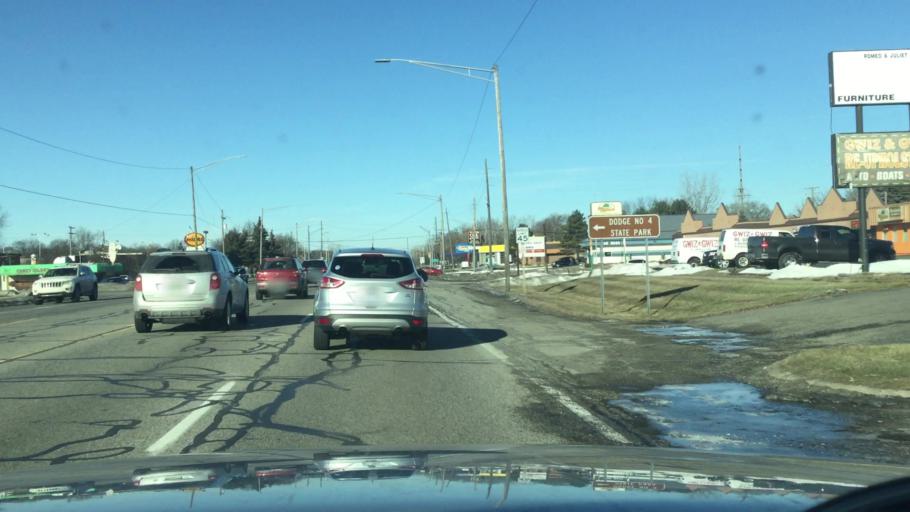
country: US
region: Michigan
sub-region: Oakland County
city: Keego Harbor
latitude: 42.6401
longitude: -83.3530
